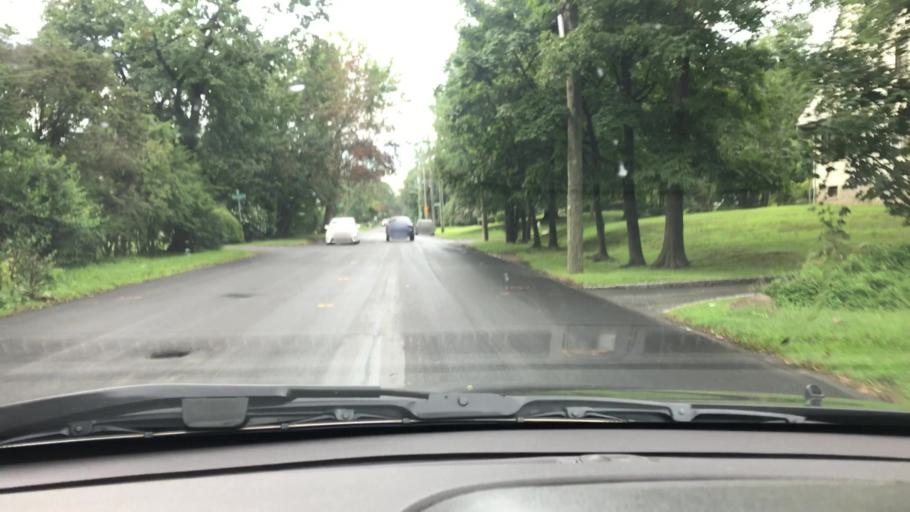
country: US
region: New York
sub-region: Westchester County
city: Pelham
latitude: 40.9363
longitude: -73.7979
